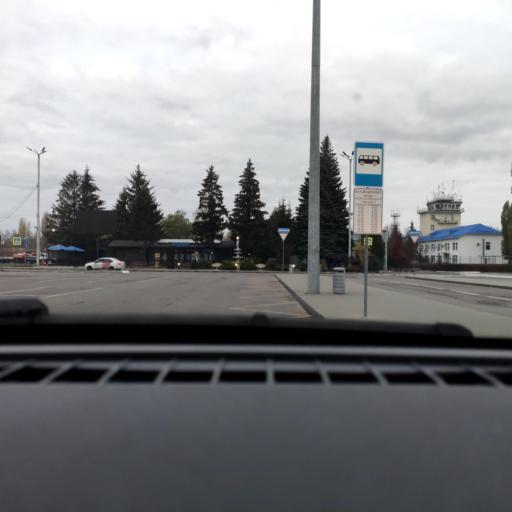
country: RU
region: Voronezj
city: Podgornoye
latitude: 51.8123
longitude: 39.2250
